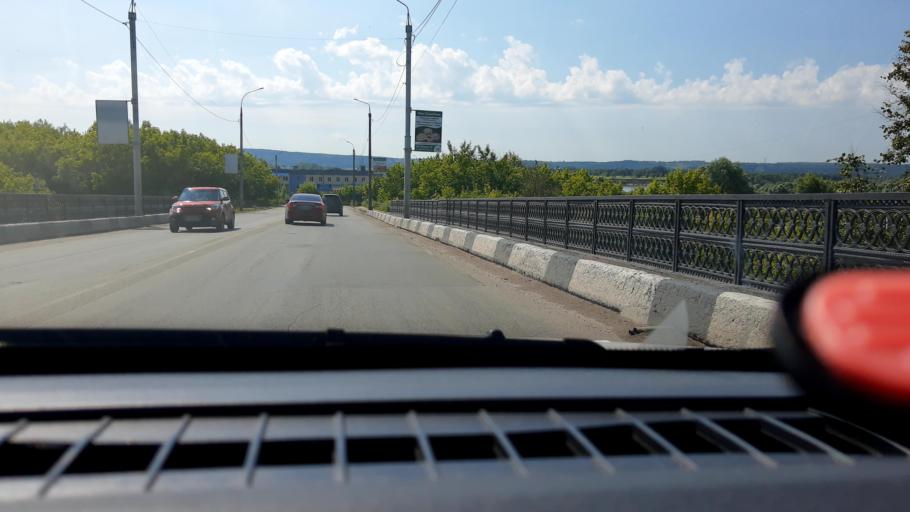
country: RU
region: Nizjnij Novgorod
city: Dzerzhinsk
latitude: 56.2339
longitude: 43.4899
